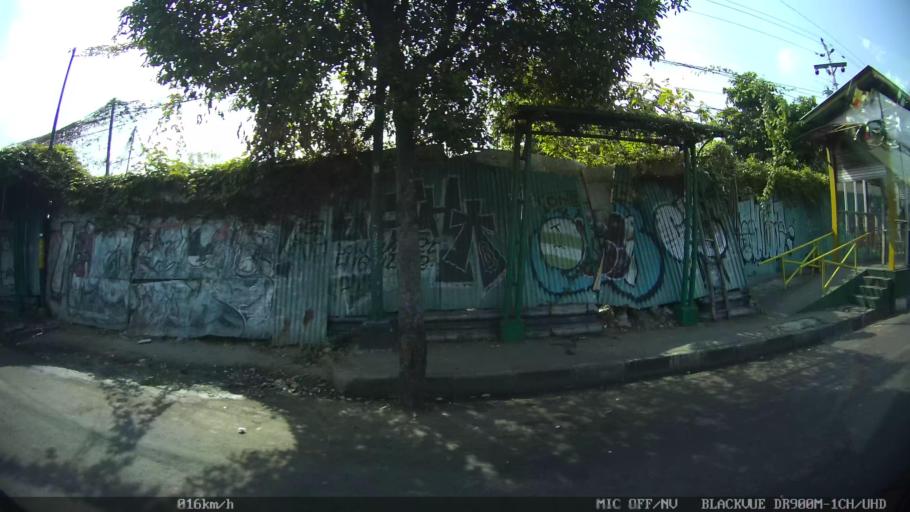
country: ID
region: Daerah Istimewa Yogyakarta
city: Yogyakarta
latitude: -7.8084
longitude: 110.3693
